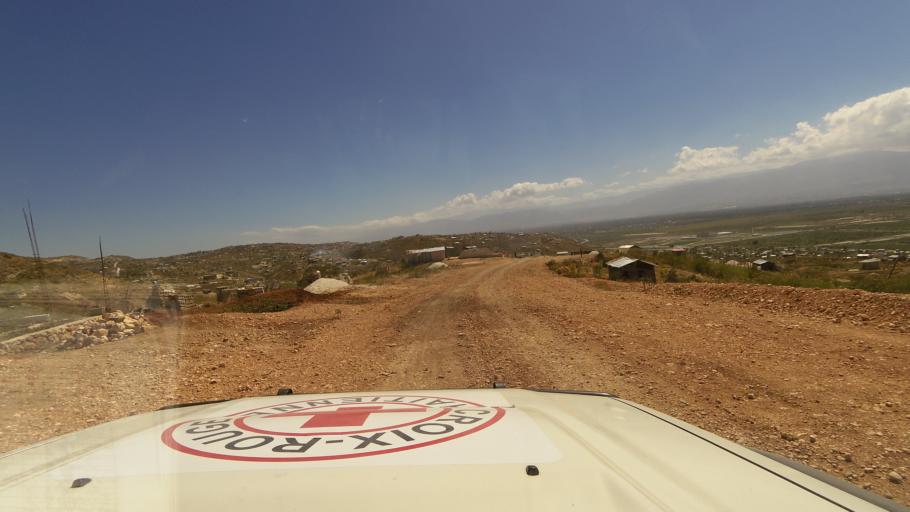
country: HT
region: Ouest
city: Croix des Bouquets
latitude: 18.6712
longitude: -72.2953
